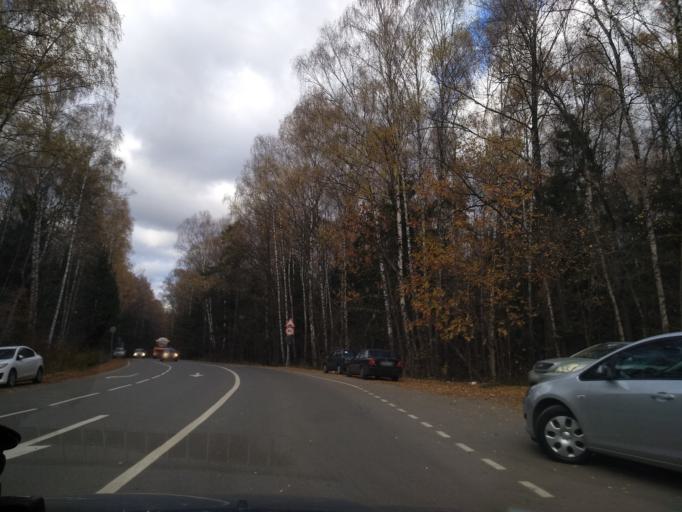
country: RU
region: Moscow
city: Bibirevo
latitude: 55.9074
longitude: 37.6120
